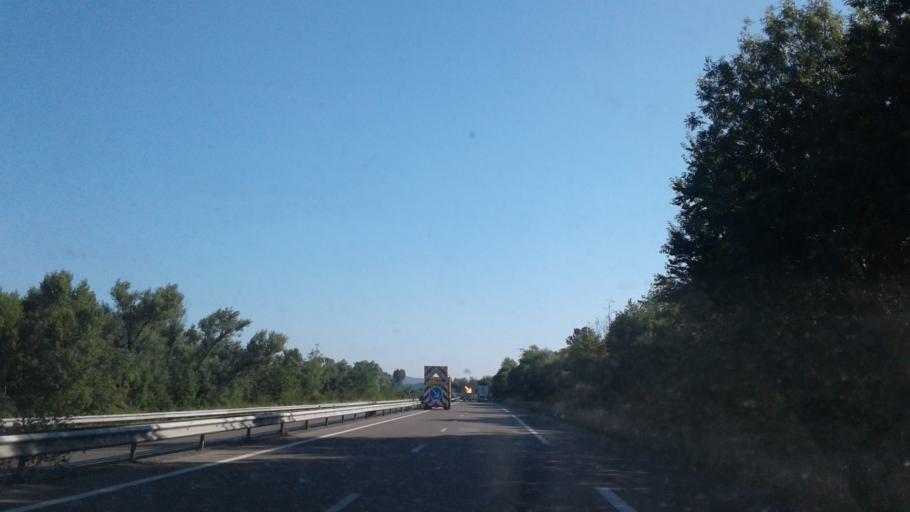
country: FR
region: Rhone-Alpes
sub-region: Departement de l'Ain
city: Priay
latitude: 46.0369
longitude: 5.3211
